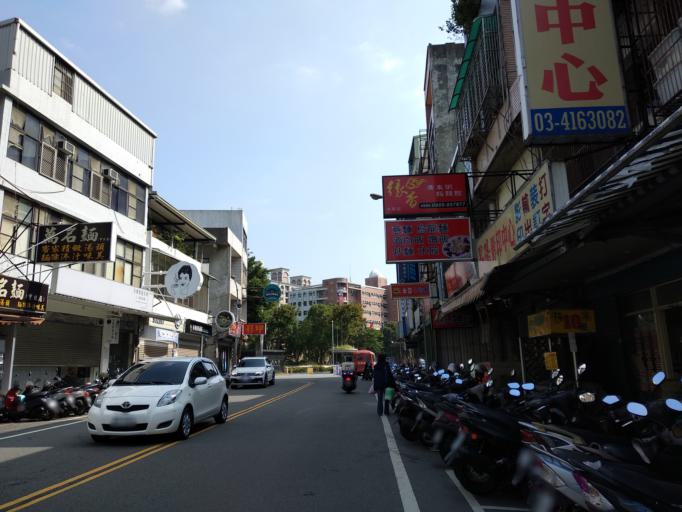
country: TW
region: Taiwan
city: Taoyuan City
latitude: 24.9571
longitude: 121.2398
